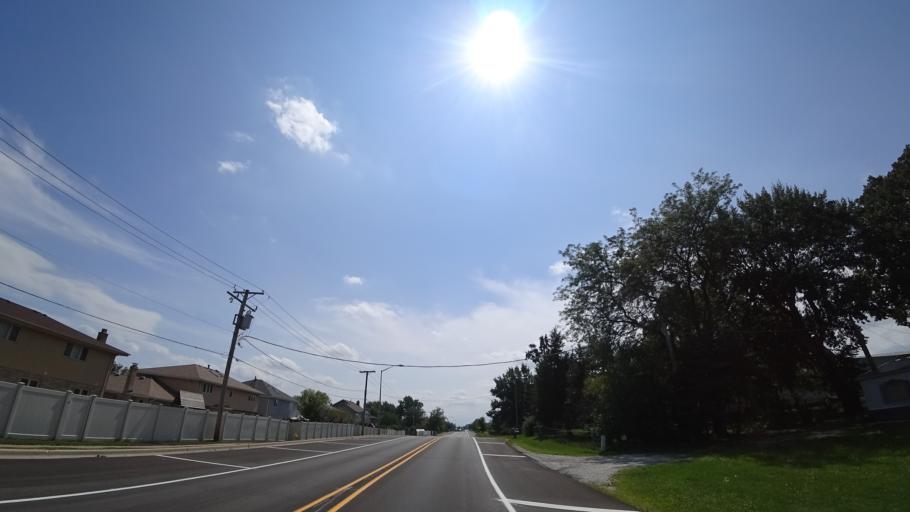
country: US
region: Illinois
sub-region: Cook County
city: Orland Hills
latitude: 41.5705
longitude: -87.8224
